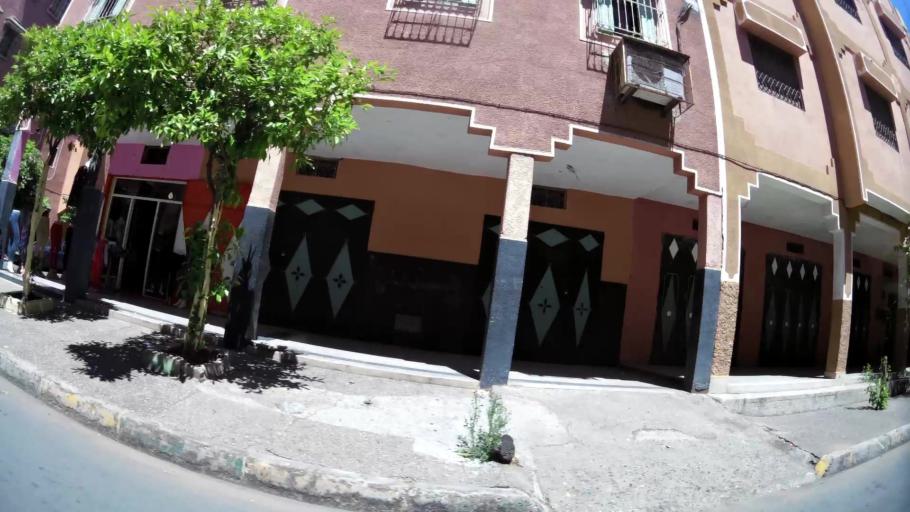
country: MA
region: Marrakech-Tensift-Al Haouz
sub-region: Marrakech
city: Marrakesh
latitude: 31.6311
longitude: -8.0530
